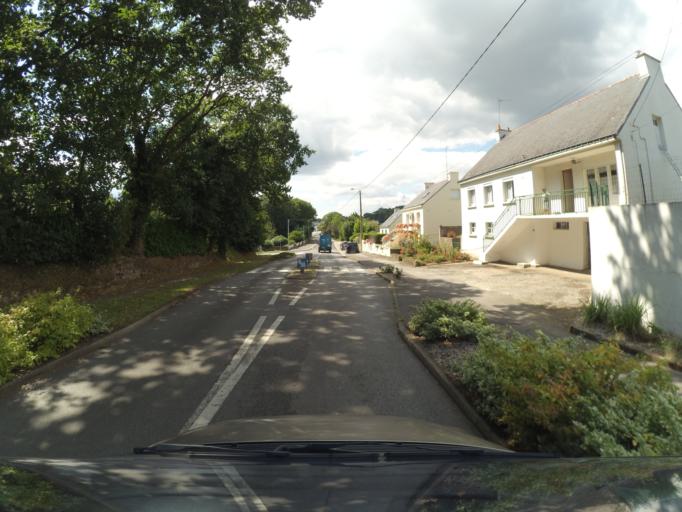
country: FR
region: Brittany
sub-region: Departement du Morbihan
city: Nostang
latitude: 47.7497
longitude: -3.1810
